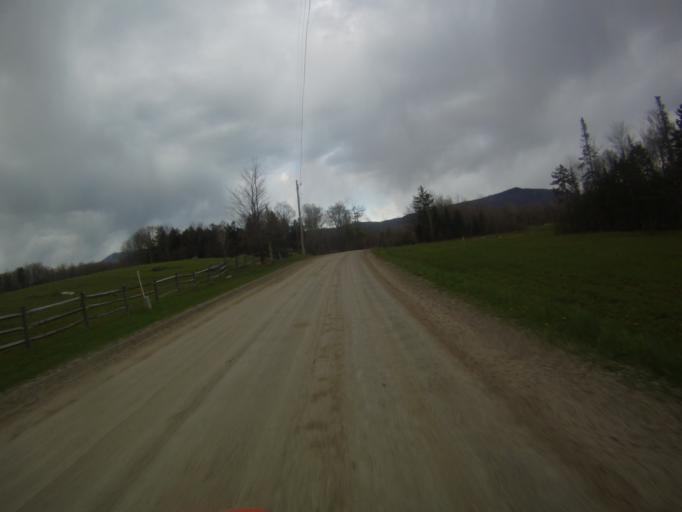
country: US
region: Vermont
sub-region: Addison County
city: Bristol
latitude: 44.0598
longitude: -73.0116
